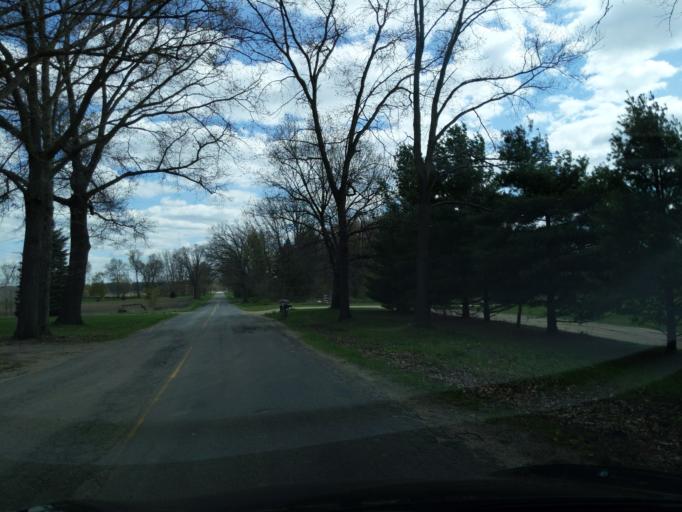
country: US
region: Michigan
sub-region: Ingham County
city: Leslie
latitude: 42.4474
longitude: -84.5263
